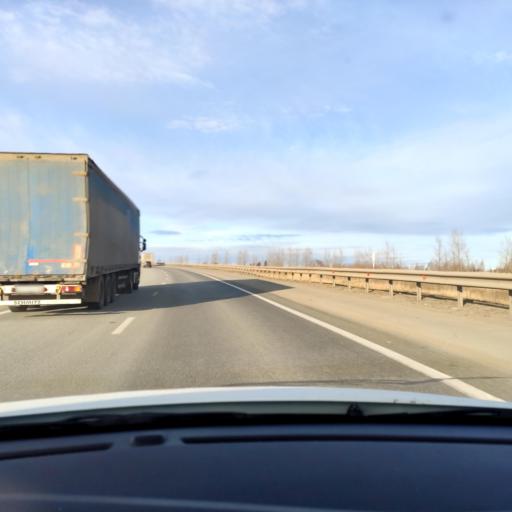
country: RU
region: Tatarstan
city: Vysokaya Gora
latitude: 55.7532
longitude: 49.3907
